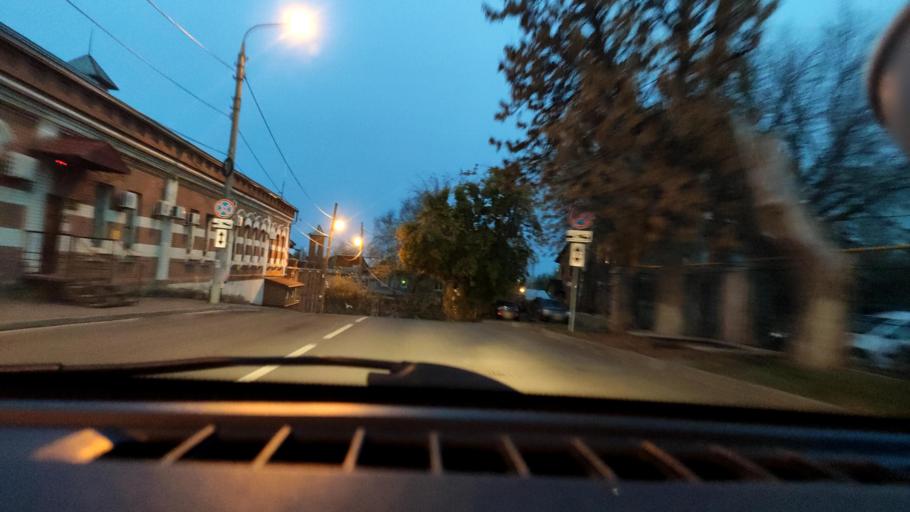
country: RU
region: Samara
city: Samara
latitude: 53.1808
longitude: 50.0957
